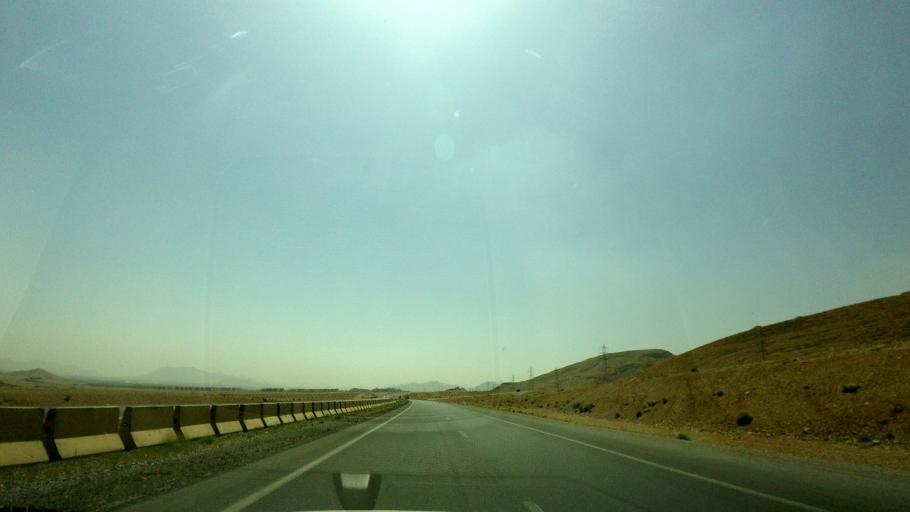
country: IR
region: Isfahan
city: Najafabad
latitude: 32.5408
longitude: 51.3158
